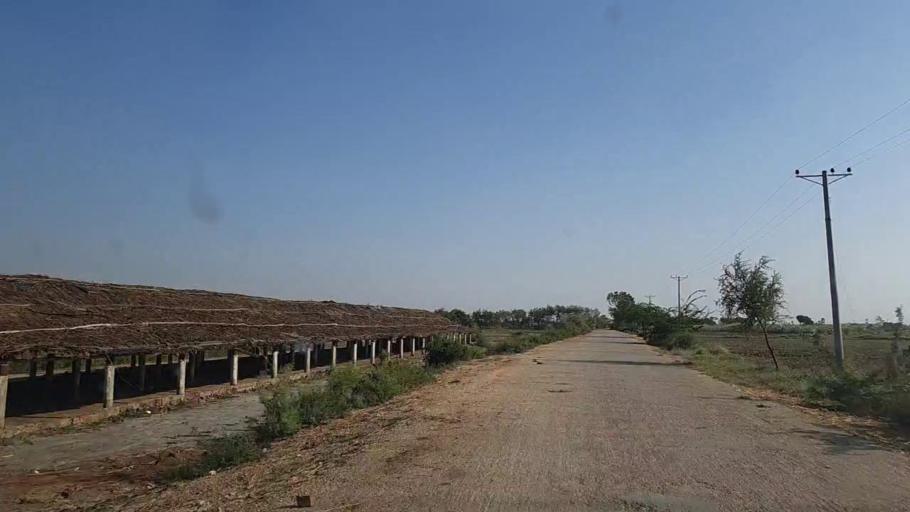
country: PK
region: Sindh
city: Thatta
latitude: 24.6339
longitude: 68.0770
